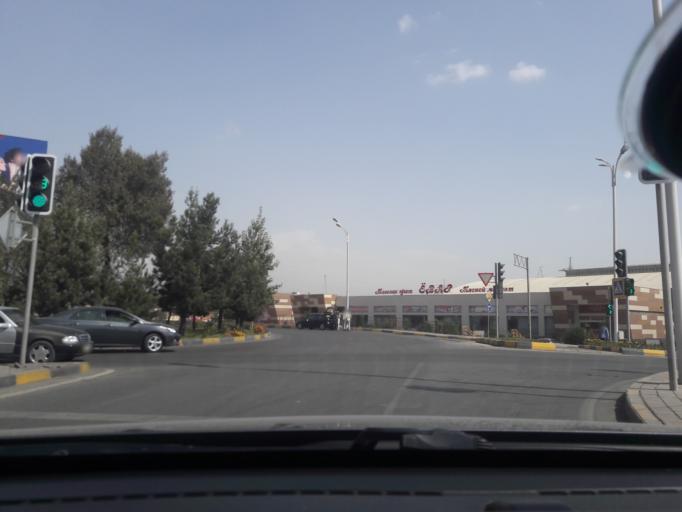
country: TJ
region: Dushanbe
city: Dushanbe
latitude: 38.5677
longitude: 68.7651
